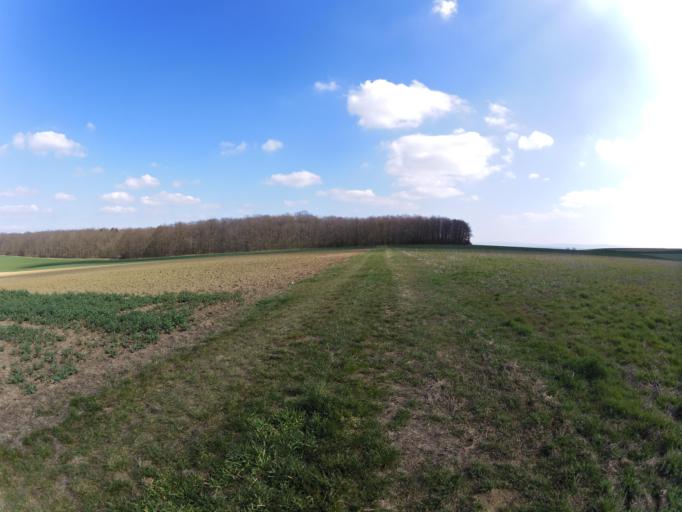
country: DE
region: Bavaria
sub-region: Regierungsbezirk Unterfranken
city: Nordheim
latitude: 49.8400
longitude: 10.1595
